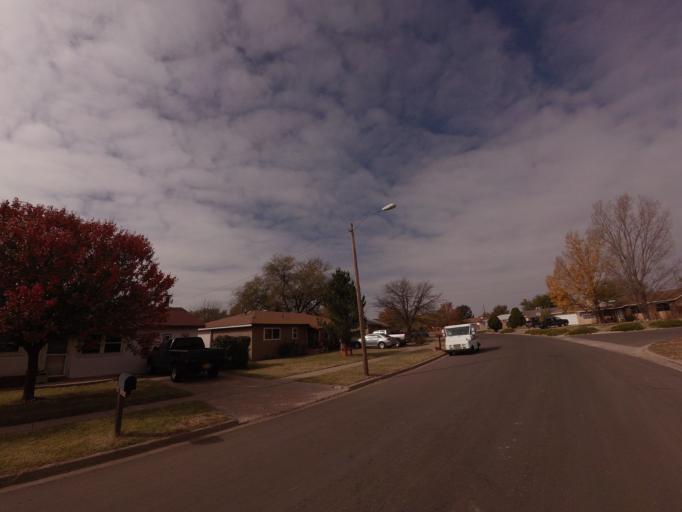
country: US
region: New Mexico
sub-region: Curry County
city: Clovis
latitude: 34.4310
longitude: -103.2182
